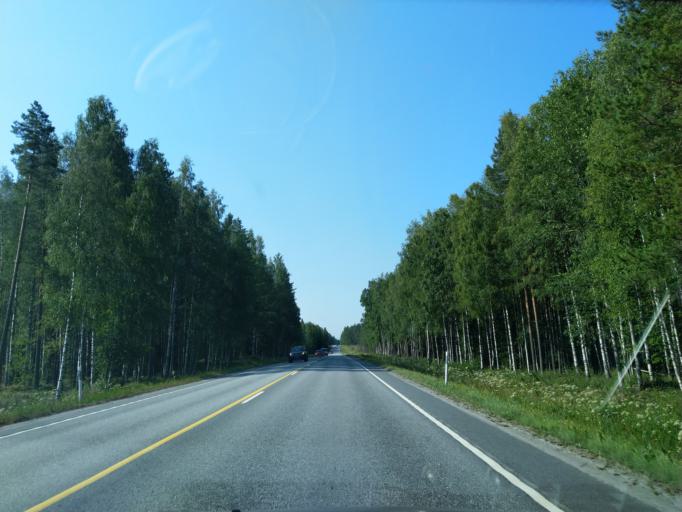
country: FI
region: Satakunta
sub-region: Pori
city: Pomarkku
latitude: 61.6693
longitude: 21.9775
